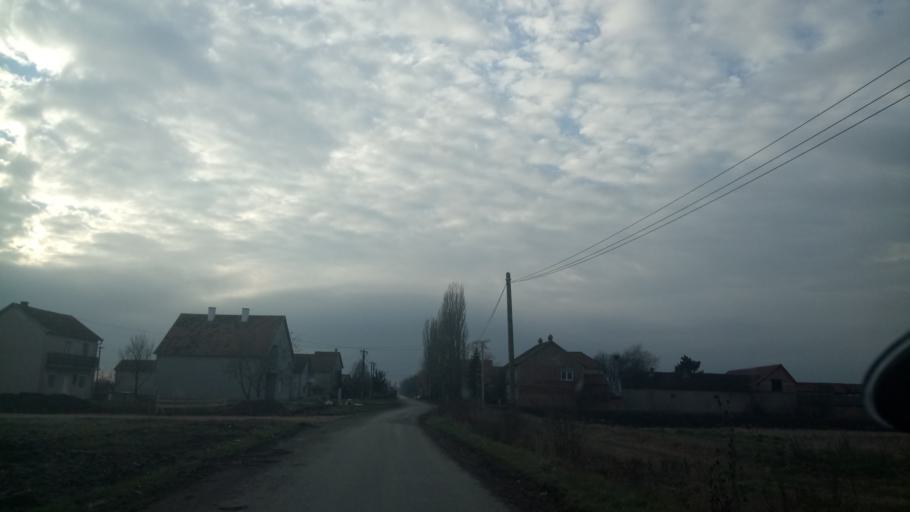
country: RS
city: Vojka
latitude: 44.9315
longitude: 20.1640
